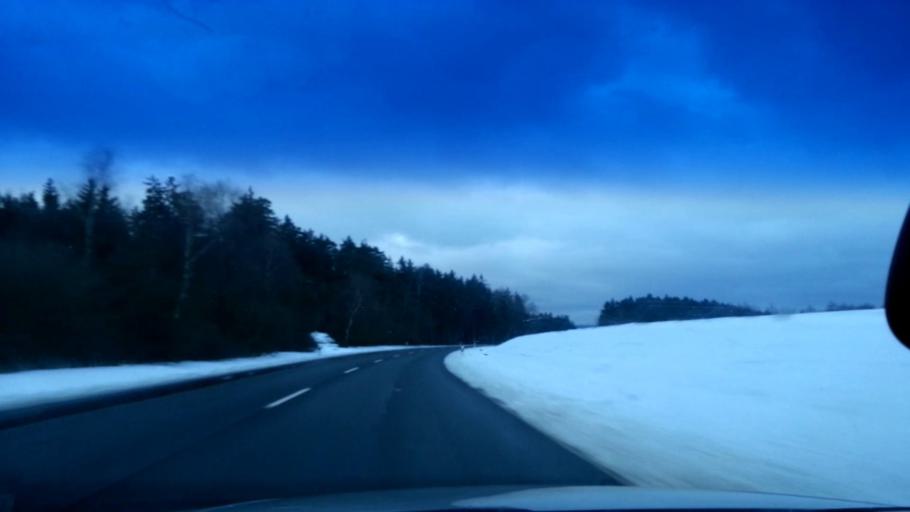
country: DE
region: Bavaria
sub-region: Upper Franconia
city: Marktleuthen
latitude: 50.1535
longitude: 12.0353
